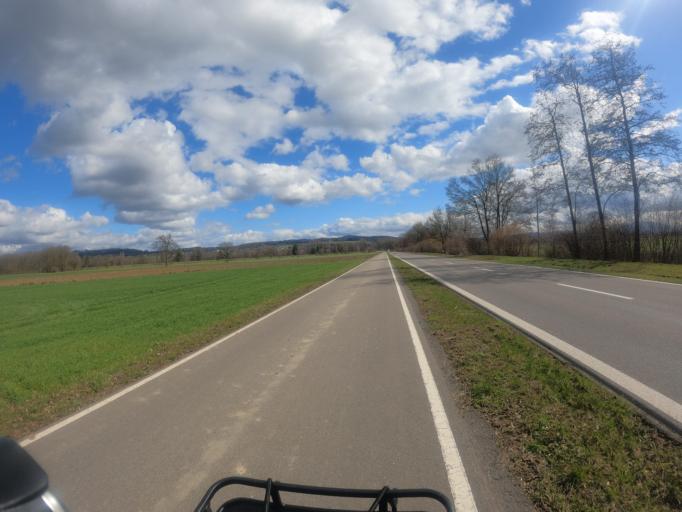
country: CH
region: Aargau
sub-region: Bezirk Bremgarten
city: Jonen
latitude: 47.2802
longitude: 8.3840
